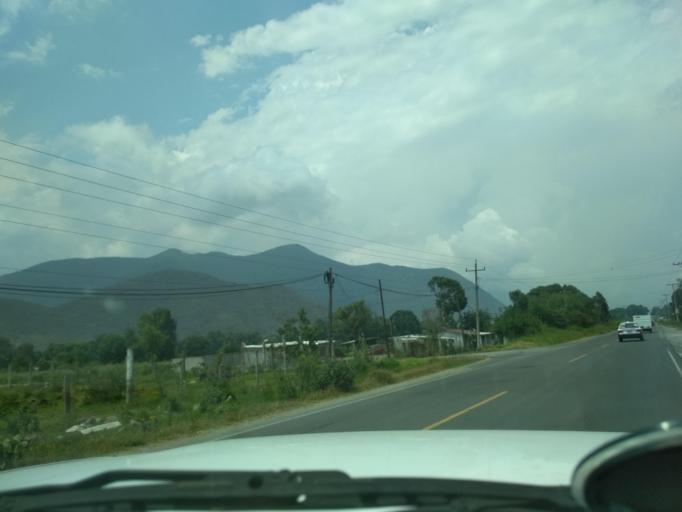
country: MX
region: Veracruz
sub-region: Nogales
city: Taza de Agua Ojo Zarco
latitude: 18.7721
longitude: -97.2156
